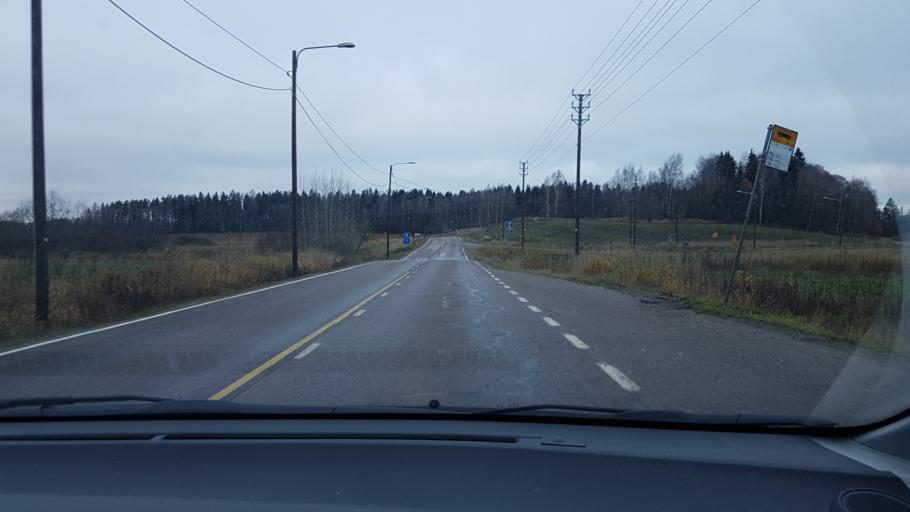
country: FI
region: Uusimaa
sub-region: Helsinki
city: Vantaa
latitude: 60.2755
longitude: 25.1376
